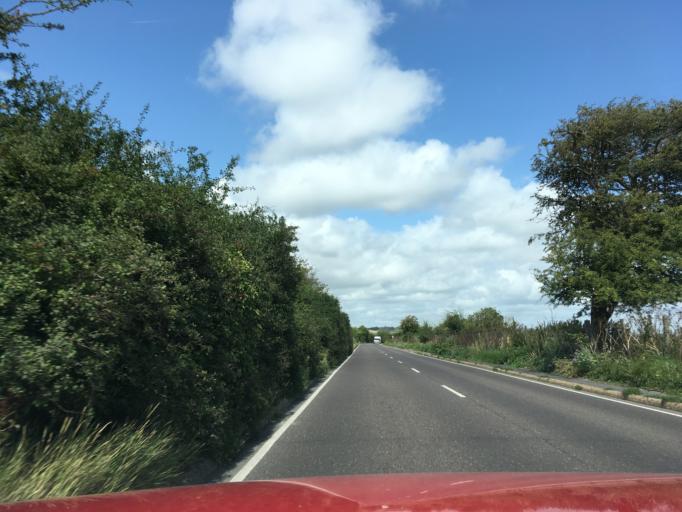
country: GB
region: England
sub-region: East Sussex
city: Rye
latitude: 50.9370
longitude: 0.7253
